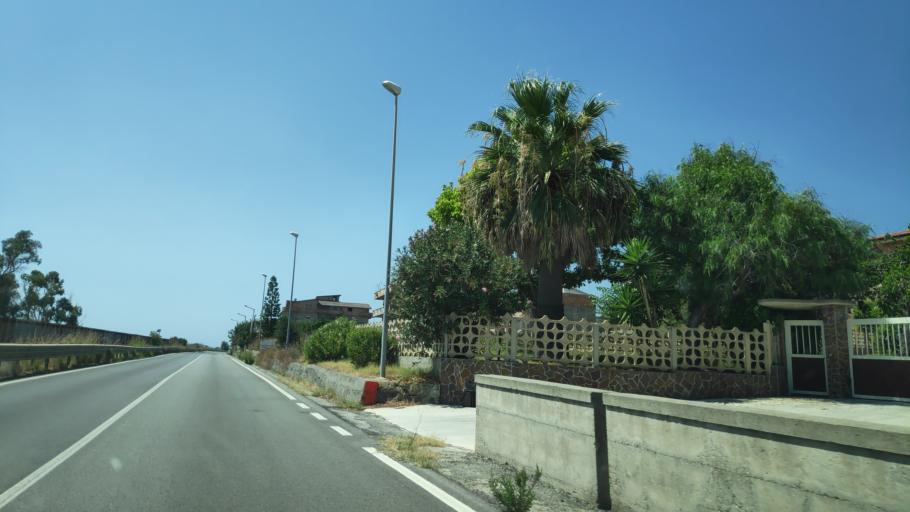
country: IT
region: Calabria
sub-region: Provincia di Reggio Calabria
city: Brancaleone-Marina
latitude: 37.9937
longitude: 16.1214
